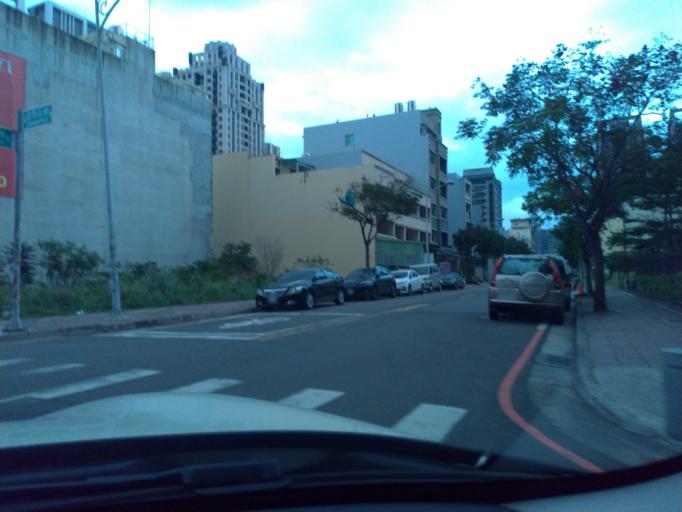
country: TW
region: Taiwan
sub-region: Hsinchu
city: Zhubei
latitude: 24.8269
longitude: 121.0285
